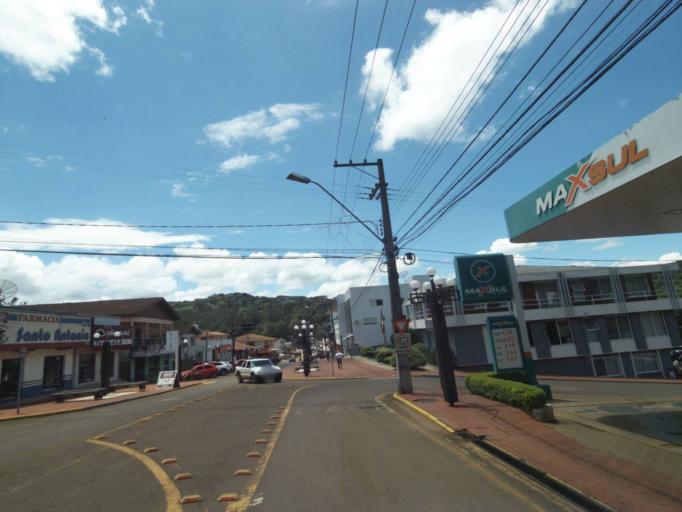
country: BR
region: Parana
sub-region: Uniao Da Vitoria
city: Uniao da Vitoria
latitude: -26.1597
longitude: -51.5548
